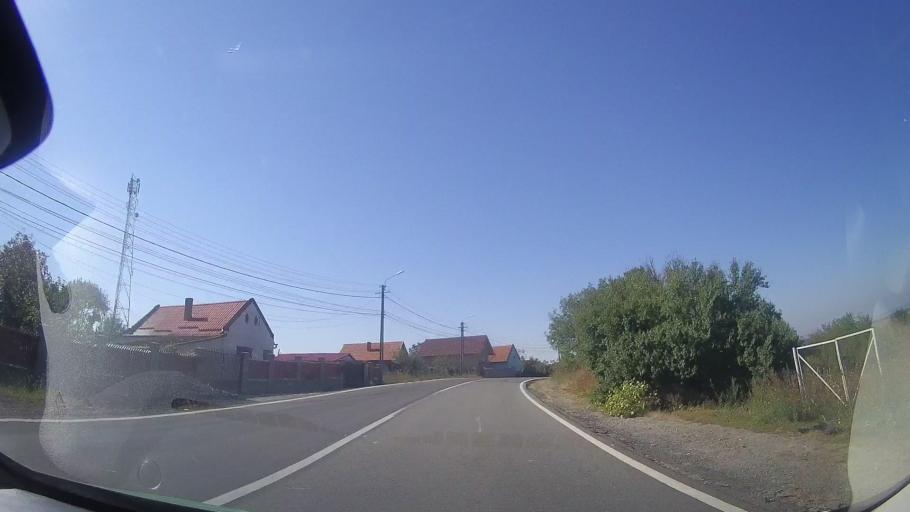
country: RO
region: Timis
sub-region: Municipiul Lugoj
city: Lugoj
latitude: 45.7037
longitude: 21.9627
